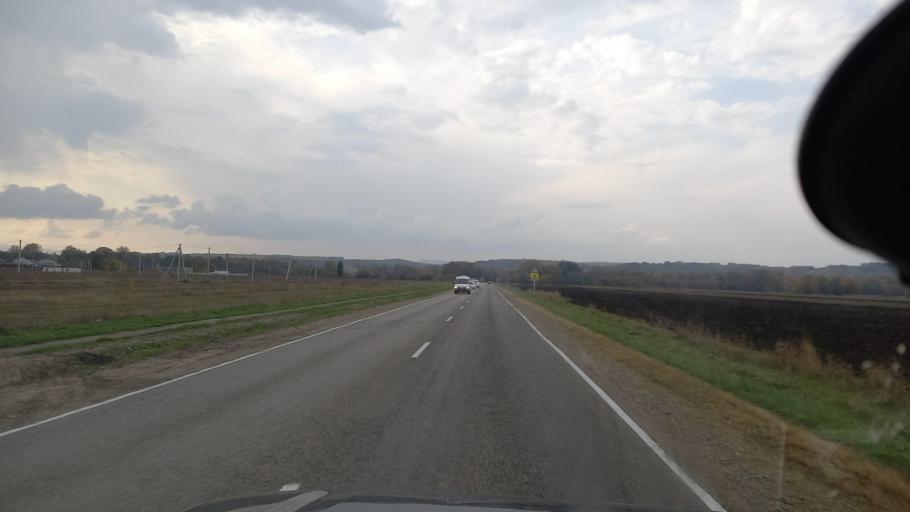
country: RU
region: Krasnodarskiy
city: Mostovskoy
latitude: 44.3922
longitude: 40.7592
